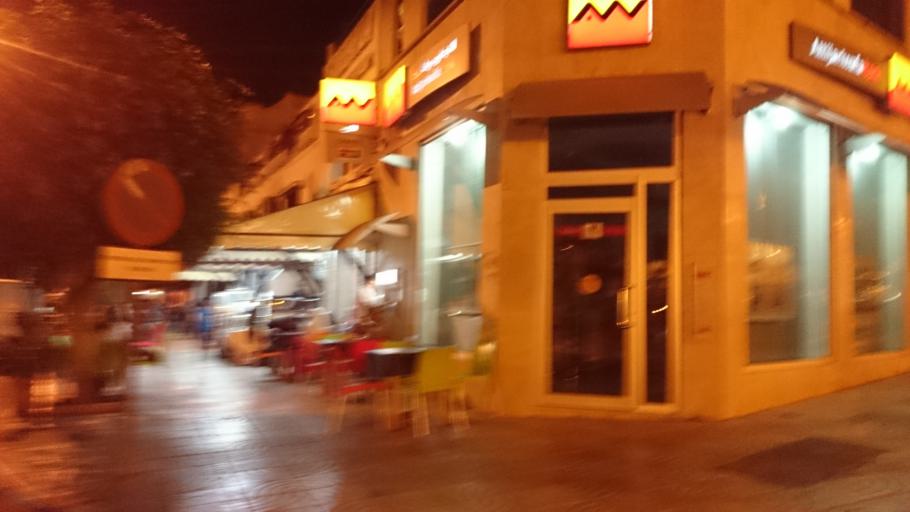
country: MA
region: Tanger-Tetouan
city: Asilah
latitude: 35.4665
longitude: -6.0332
